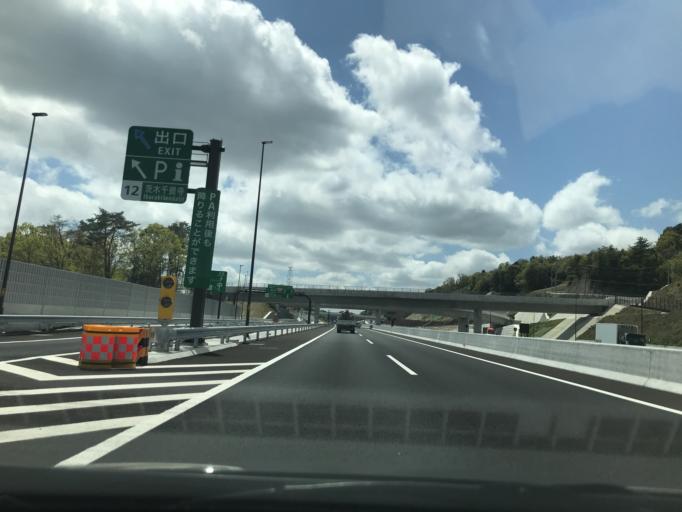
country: JP
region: Osaka
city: Ibaraki
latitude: 34.8858
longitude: 135.5365
